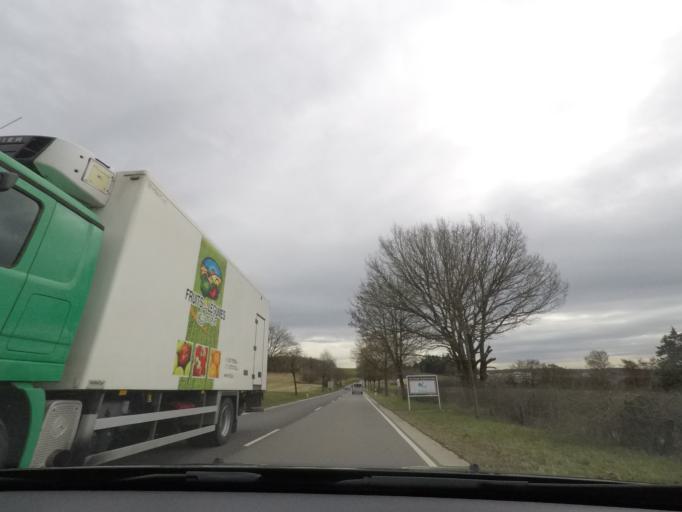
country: LU
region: Diekirch
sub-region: Canton de Wiltz
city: Winseler
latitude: 49.9802
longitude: 5.8402
